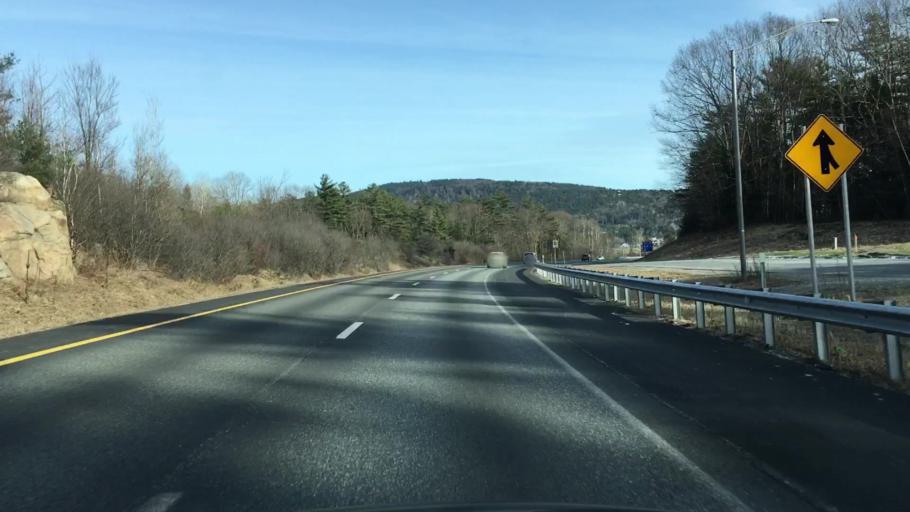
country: US
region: New Hampshire
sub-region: Grafton County
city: Lebanon
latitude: 43.6501
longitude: -72.2602
